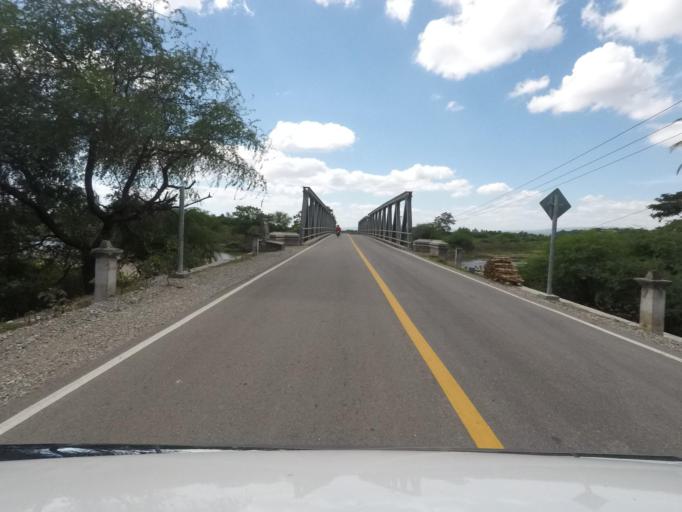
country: TL
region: Baucau
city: Baucau
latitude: -8.4087
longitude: 126.7298
